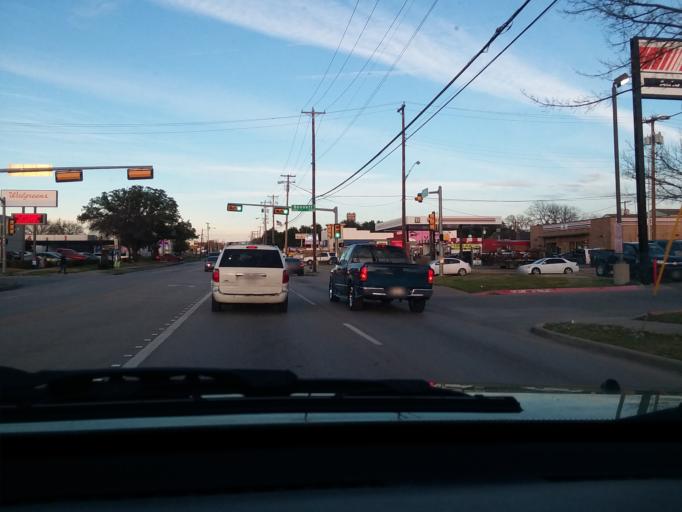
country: US
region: Texas
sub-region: Dallas County
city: Highland Park
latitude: 32.8068
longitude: -96.7755
